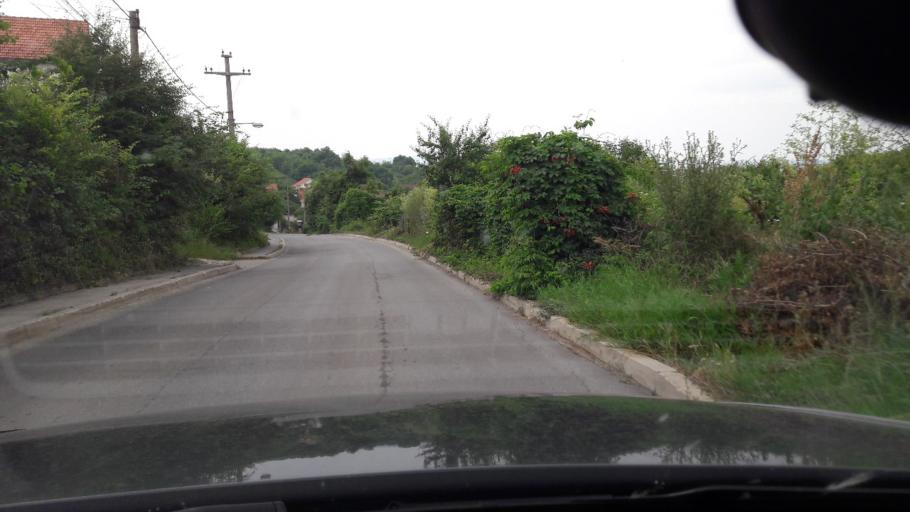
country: RS
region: Central Serbia
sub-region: Belgrade
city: Grocka
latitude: 44.6562
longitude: 20.5943
